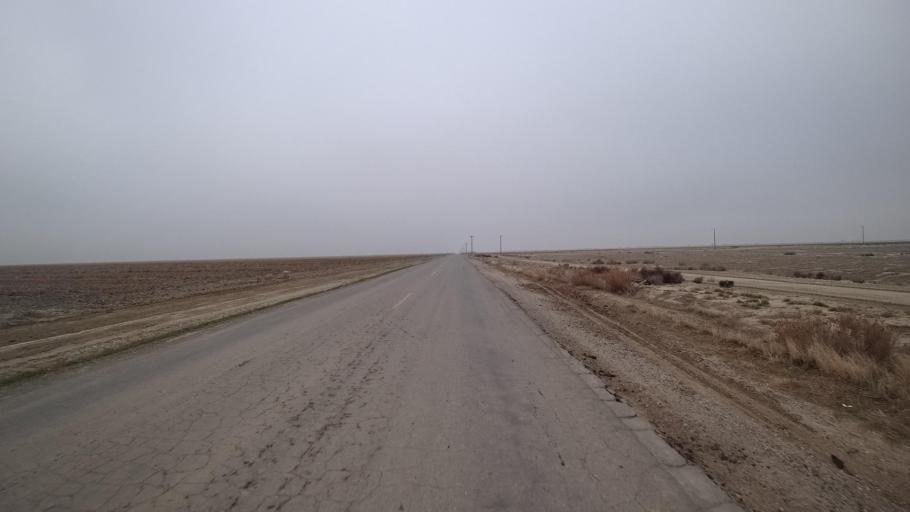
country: US
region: California
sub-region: Kern County
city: Rosedale
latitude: 35.2326
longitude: -119.2328
